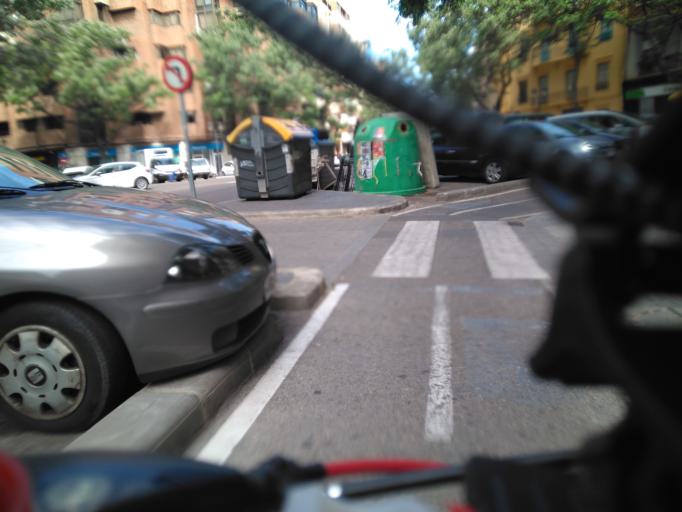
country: ES
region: Valencia
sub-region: Provincia de Valencia
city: Valencia
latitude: 39.4708
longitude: -0.3894
